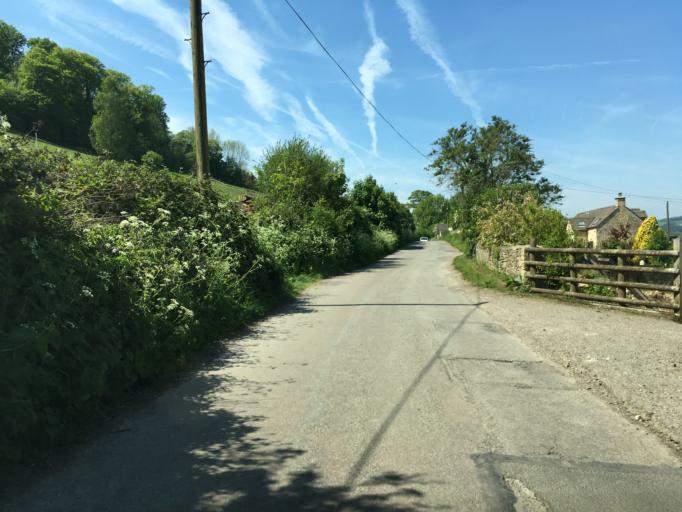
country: GB
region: England
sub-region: Gloucestershire
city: Stroud
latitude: 51.7366
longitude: -2.2153
